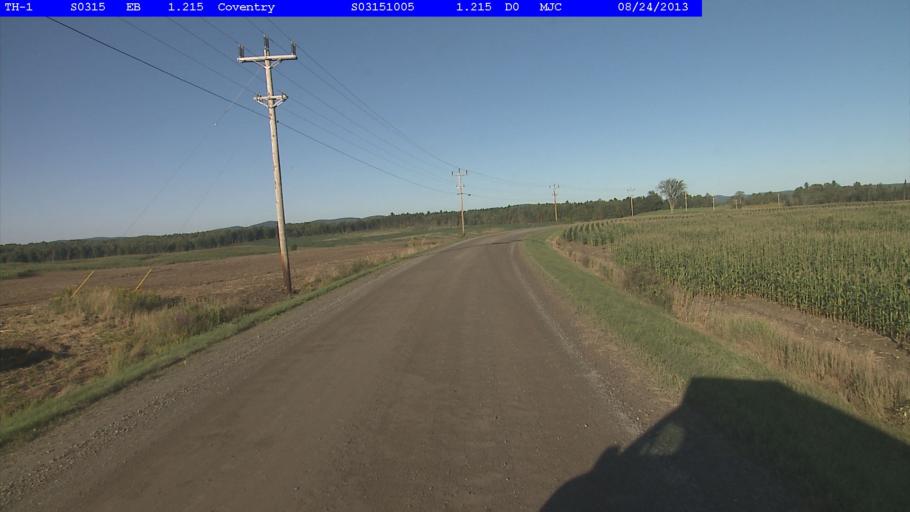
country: US
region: Vermont
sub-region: Orleans County
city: Newport
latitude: 44.8707
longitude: -72.2378
